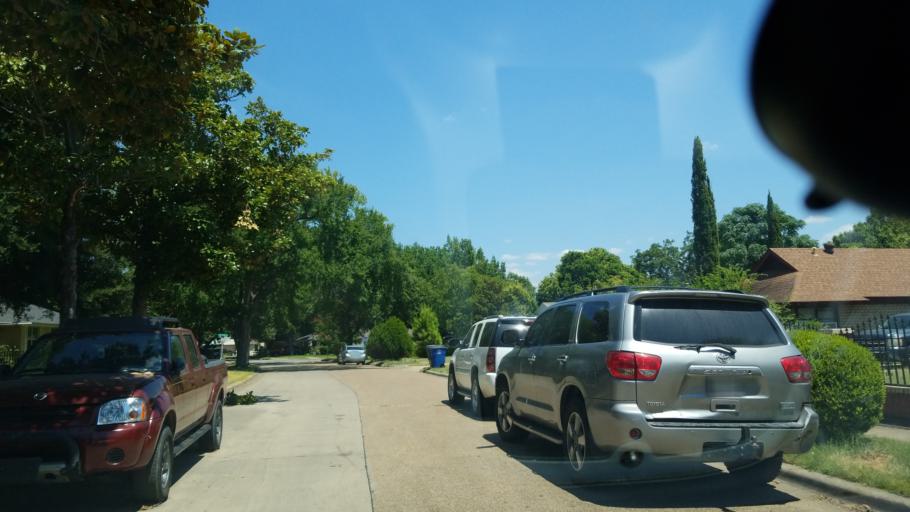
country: US
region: Texas
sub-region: Dallas County
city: Cockrell Hill
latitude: 32.7177
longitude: -96.8446
